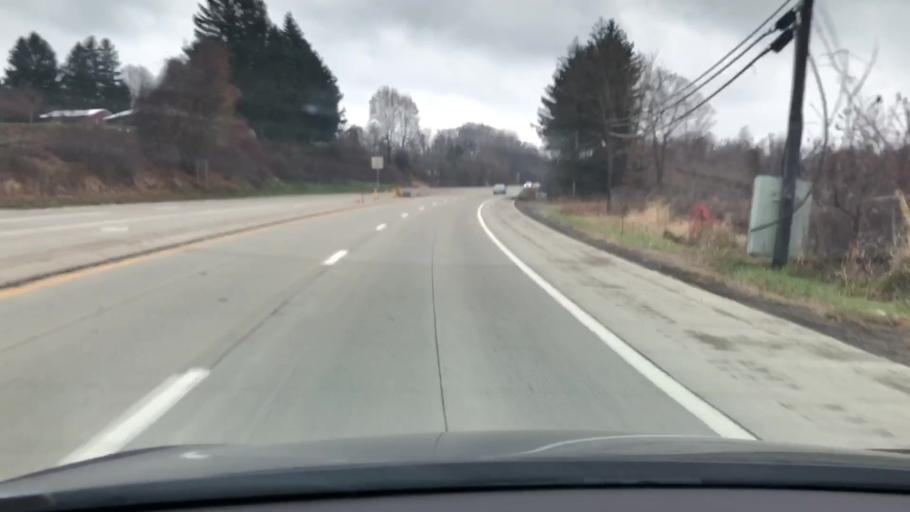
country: US
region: Pennsylvania
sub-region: Fayette County
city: Dunbar
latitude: 39.9833
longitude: -79.6308
